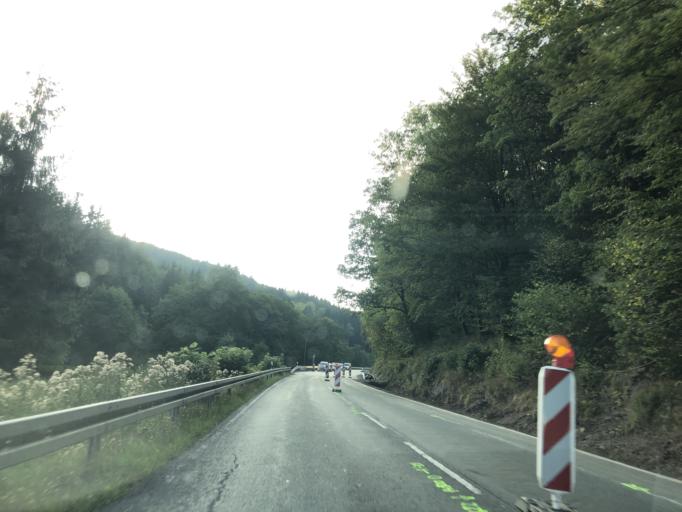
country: DE
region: North Rhine-Westphalia
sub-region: Regierungsbezirk Arnsberg
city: Winterberg
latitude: 51.1697
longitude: 8.5494
